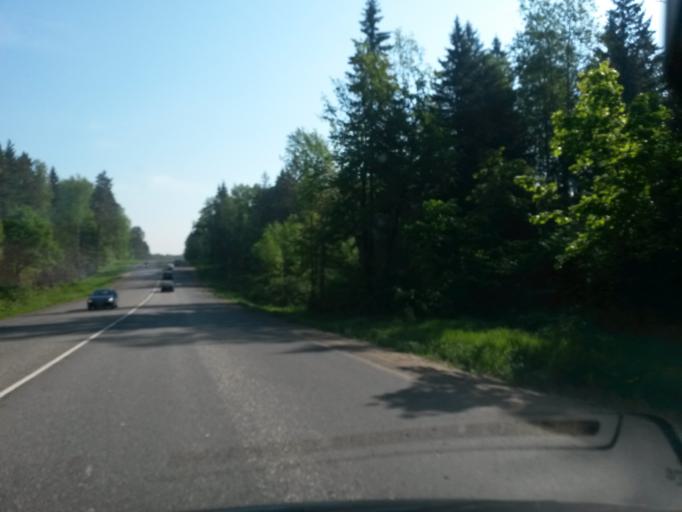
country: RU
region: Jaroslavl
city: Pereslavl'-Zalesskiy
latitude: 56.8647
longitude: 38.9575
